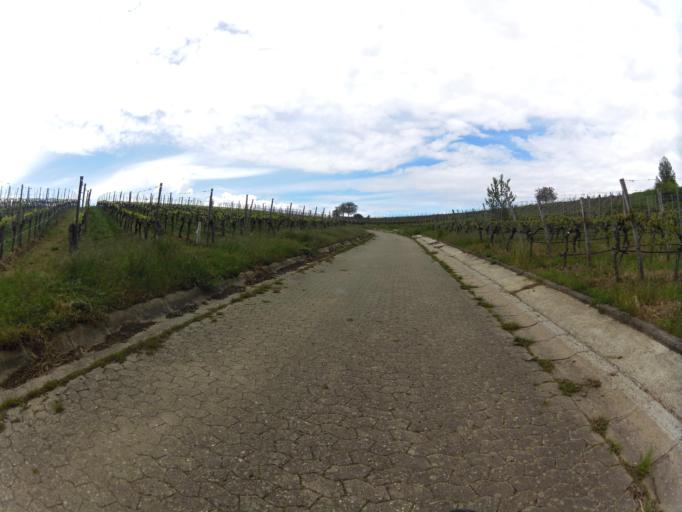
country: DE
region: Bavaria
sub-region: Regierungsbezirk Unterfranken
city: Sommerach
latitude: 49.8384
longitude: 10.1874
